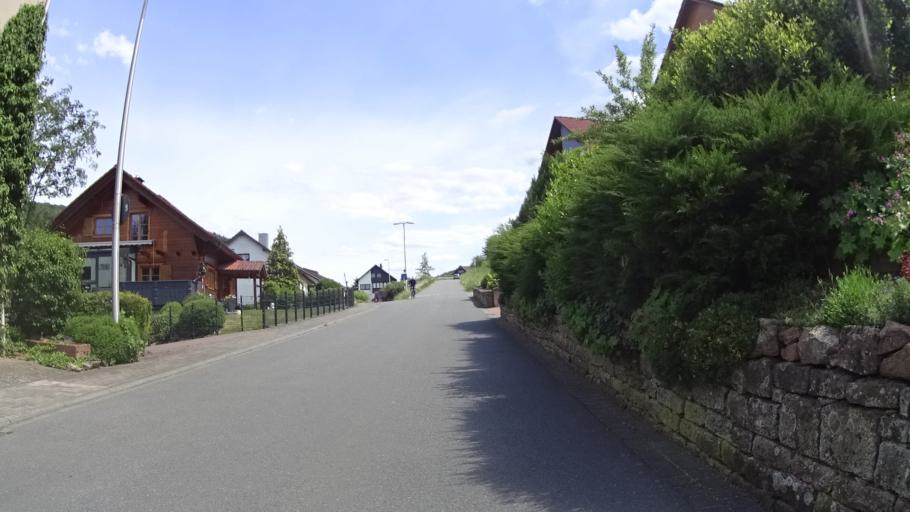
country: DE
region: Bavaria
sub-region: Regierungsbezirk Unterfranken
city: Neunkirchen
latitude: 49.6686
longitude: 9.3965
